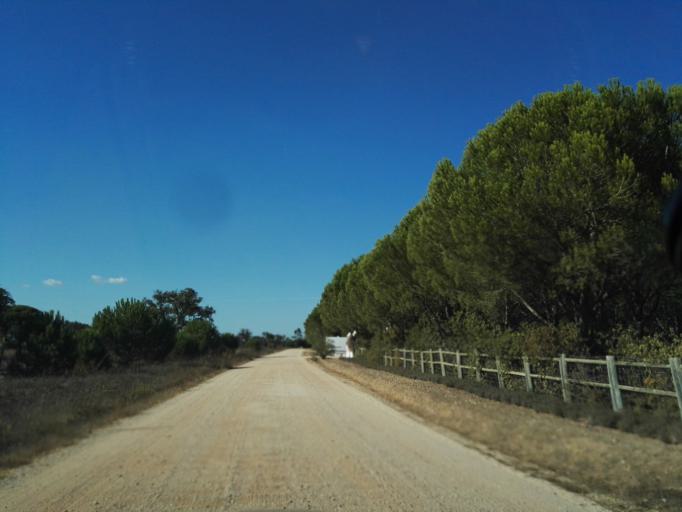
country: PT
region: Santarem
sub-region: Benavente
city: Poceirao
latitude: 38.8789
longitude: -8.7415
